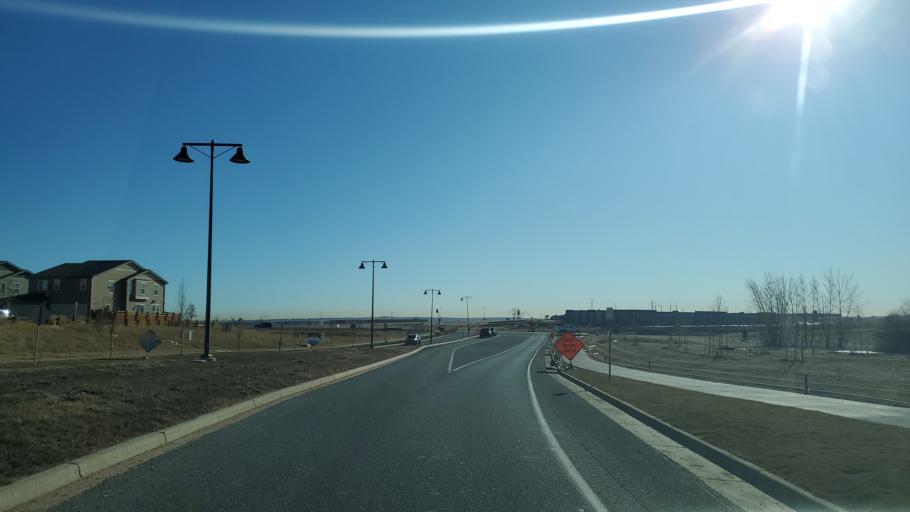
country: US
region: Colorado
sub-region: Boulder County
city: Erie
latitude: 39.9932
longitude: -105.0159
